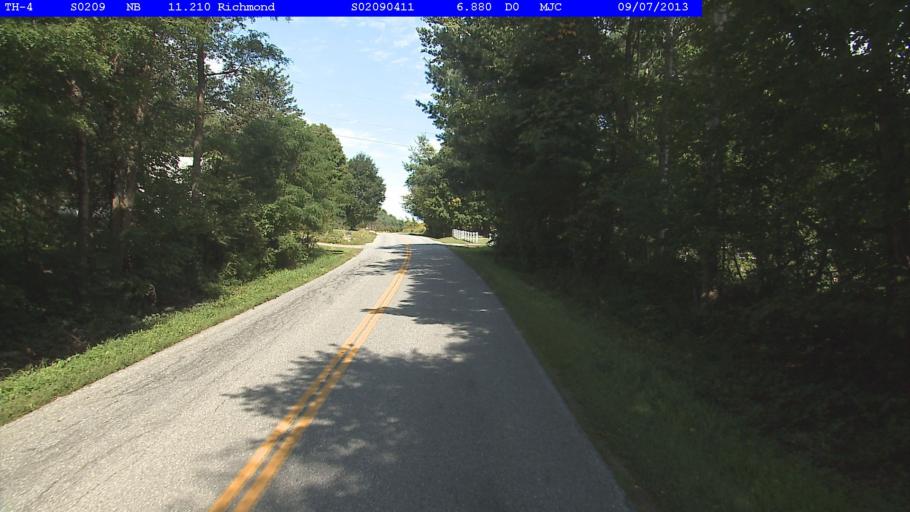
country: US
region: Vermont
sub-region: Chittenden County
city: Jericho
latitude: 44.4235
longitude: -72.9792
